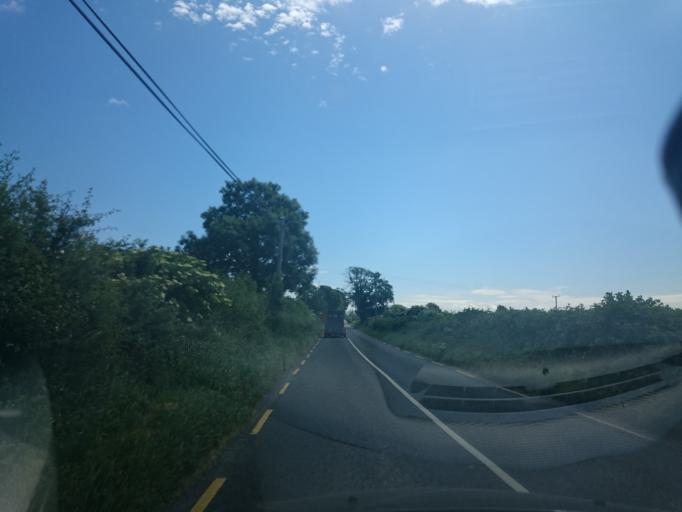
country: IE
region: Leinster
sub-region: Kilkenny
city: Thomastown
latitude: 52.6394
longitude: -7.1018
